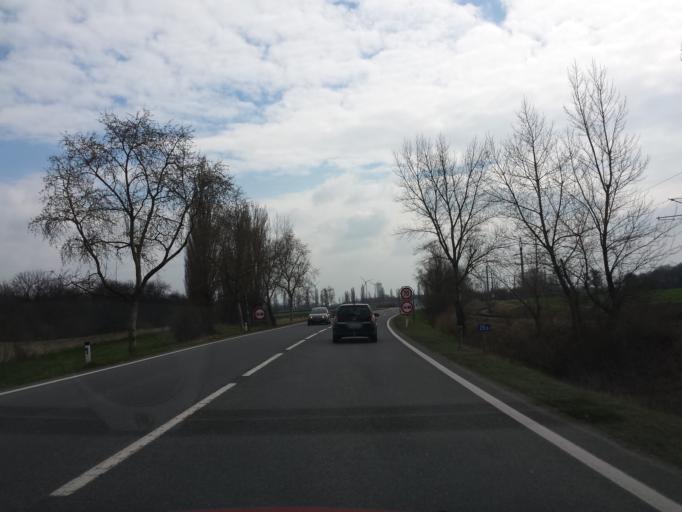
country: AT
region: Lower Austria
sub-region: Politischer Bezirk Bruck an der Leitha
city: Petronell-Carnuntum
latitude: 48.1123
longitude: 16.8421
